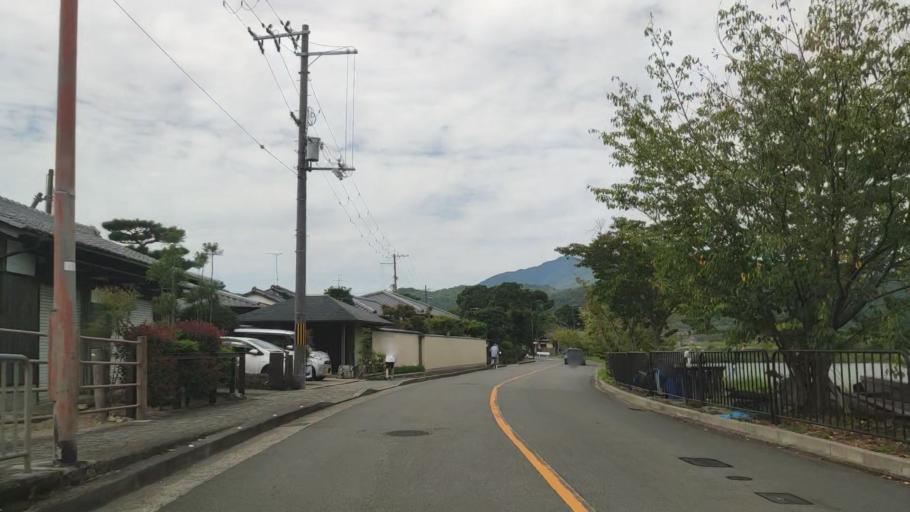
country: JP
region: Kyoto
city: Muko
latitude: 35.0253
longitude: 135.6895
